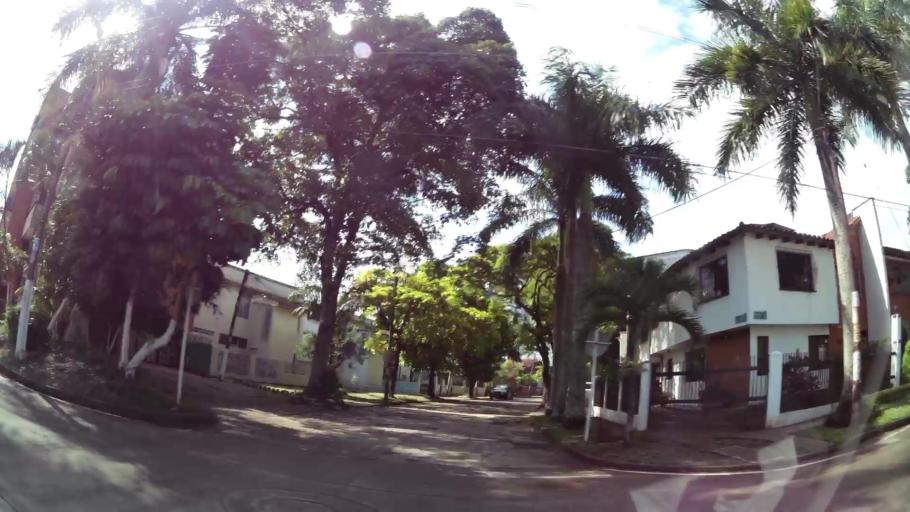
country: CO
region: Valle del Cauca
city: Cali
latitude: 3.4251
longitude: -76.5416
